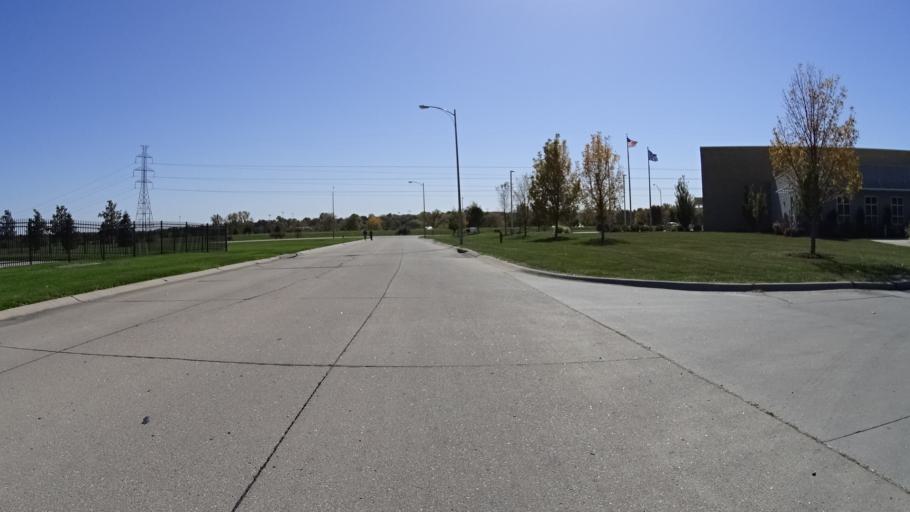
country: US
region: Nebraska
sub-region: Sarpy County
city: Papillion
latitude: 41.1570
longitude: -96.0320
